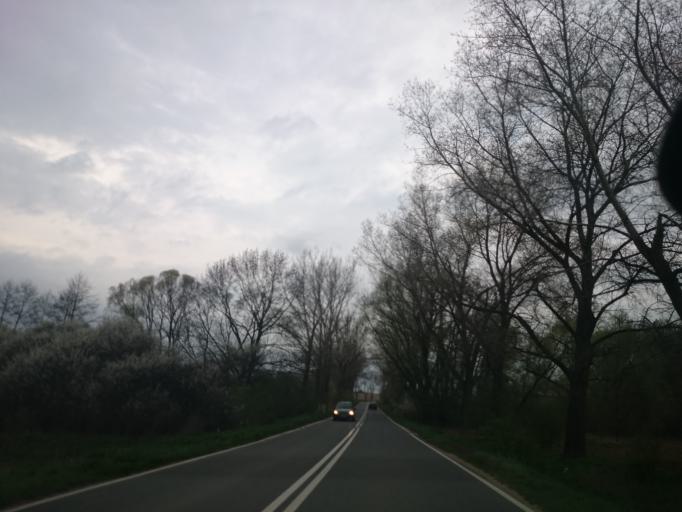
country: PL
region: Lower Silesian Voivodeship
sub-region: Powiat zabkowicki
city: Kamieniec Zabkowicki
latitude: 50.5400
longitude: 16.8646
